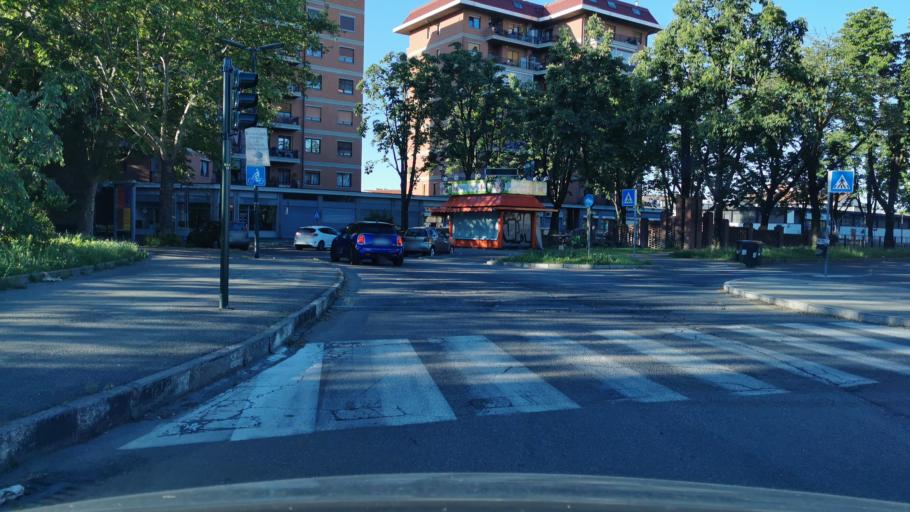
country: IT
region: Piedmont
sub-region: Provincia di Torino
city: Venaria Reale
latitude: 45.1057
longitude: 7.6546
